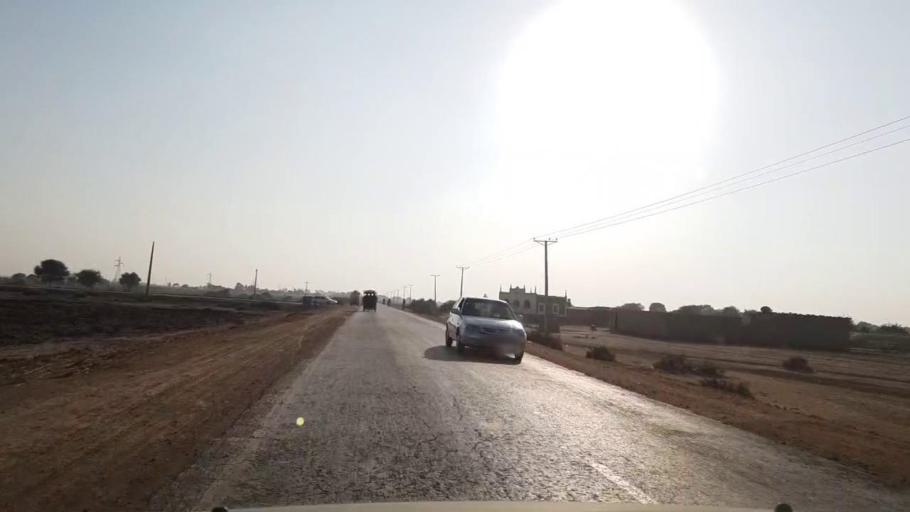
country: PK
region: Sindh
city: Mirpur Batoro
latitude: 24.7517
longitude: 68.2670
